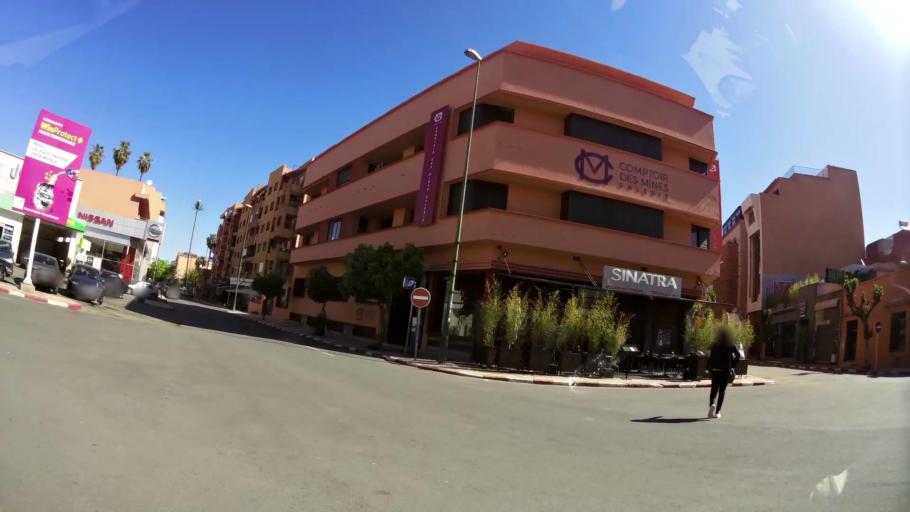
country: MA
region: Marrakech-Tensift-Al Haouz
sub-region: Marrakech
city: Marrakesh
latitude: 31.6340
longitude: -8.0138
